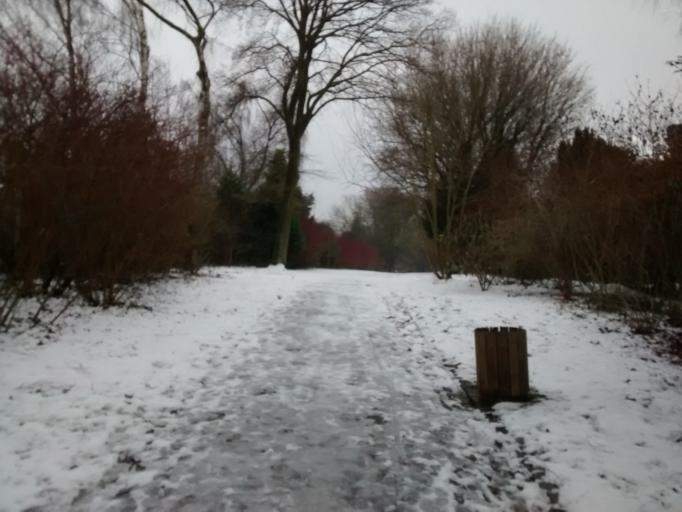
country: NL
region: Limburg
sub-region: Gemeente Vaals
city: Vaals
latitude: 50.7621
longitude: 6.0493
